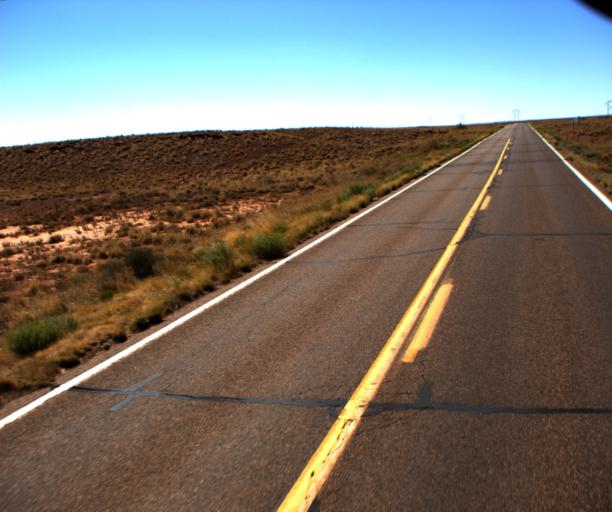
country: US
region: Arizona
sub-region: Coconino County
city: LeChee
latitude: 35.2614
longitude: -110.9683
